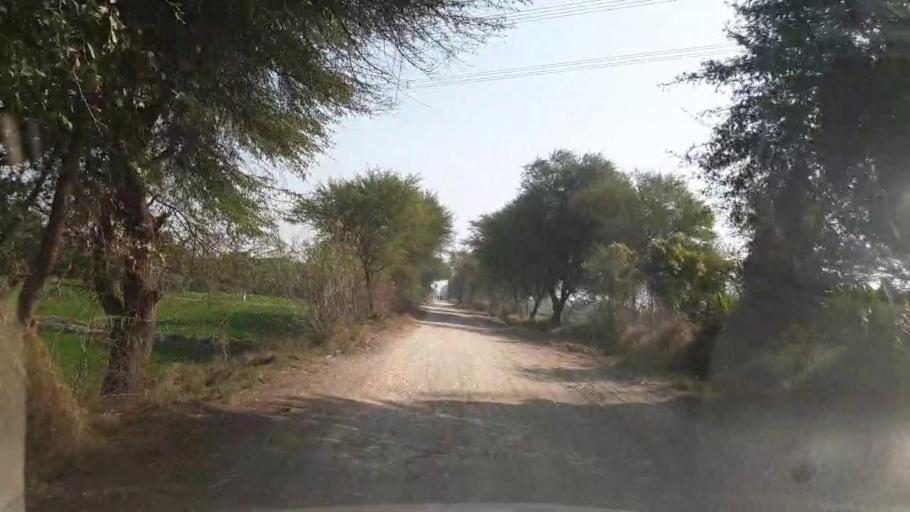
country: PK
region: Sindh
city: Matiari
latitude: 25.5444
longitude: 68.4922
